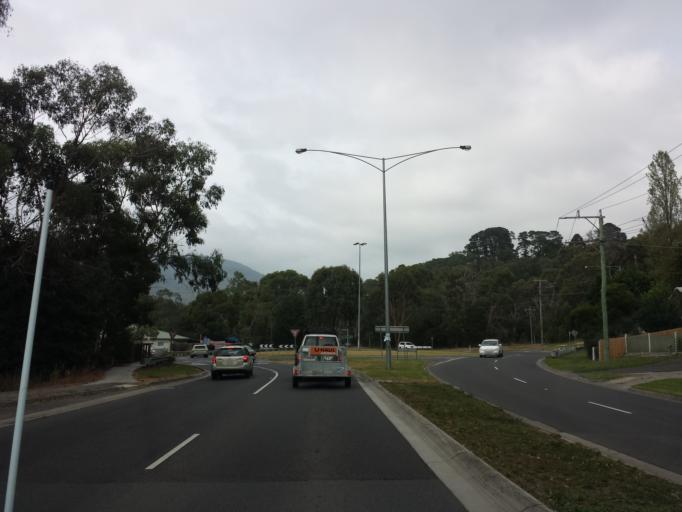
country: AU
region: Victoria
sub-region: Yarra Ranges
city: Kalorama
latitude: -37.7961
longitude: 145.3598
